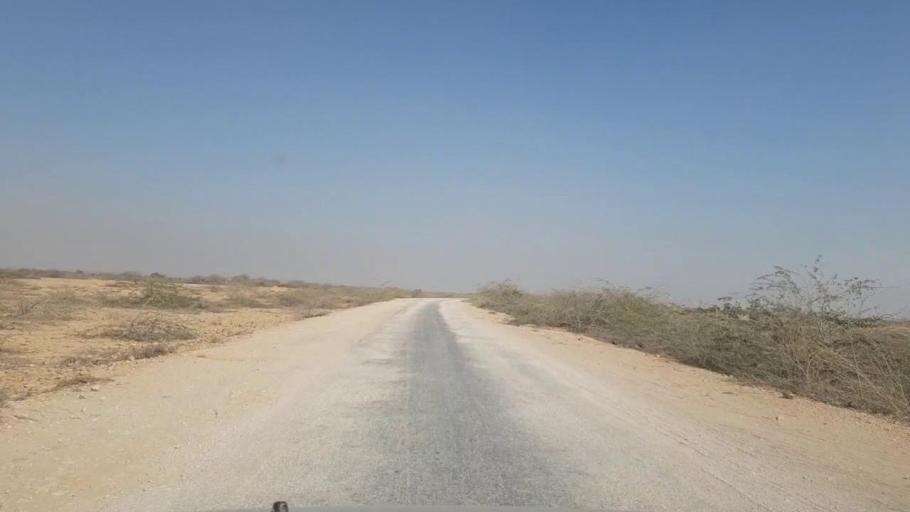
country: PK
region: Sindh
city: Thatta
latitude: 24.9022
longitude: 67.9221
